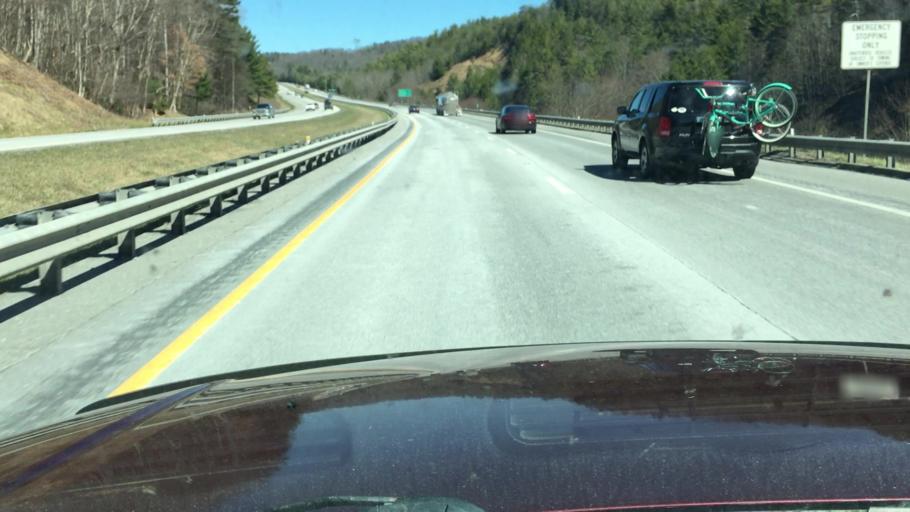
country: US
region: Virginia
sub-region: Bland County
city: Bland
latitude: 37.1127
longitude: -81.1247
